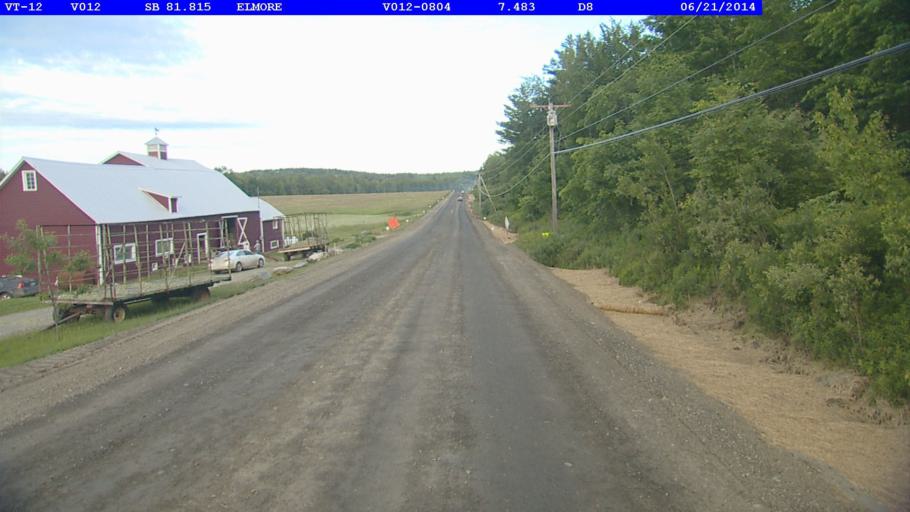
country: US
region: Vermont
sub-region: Lamoille County
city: Morrisville
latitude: 44.5485
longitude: -72.5335
